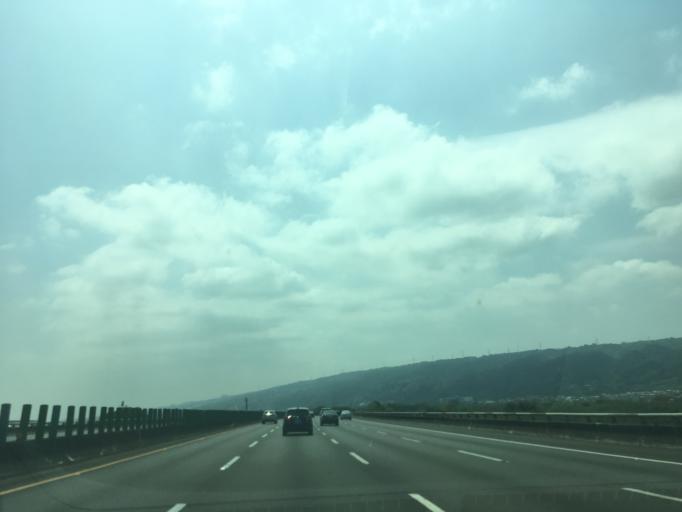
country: TW
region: Taiwan
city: Zhongxing New Village
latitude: 23.9842
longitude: 120.6526
